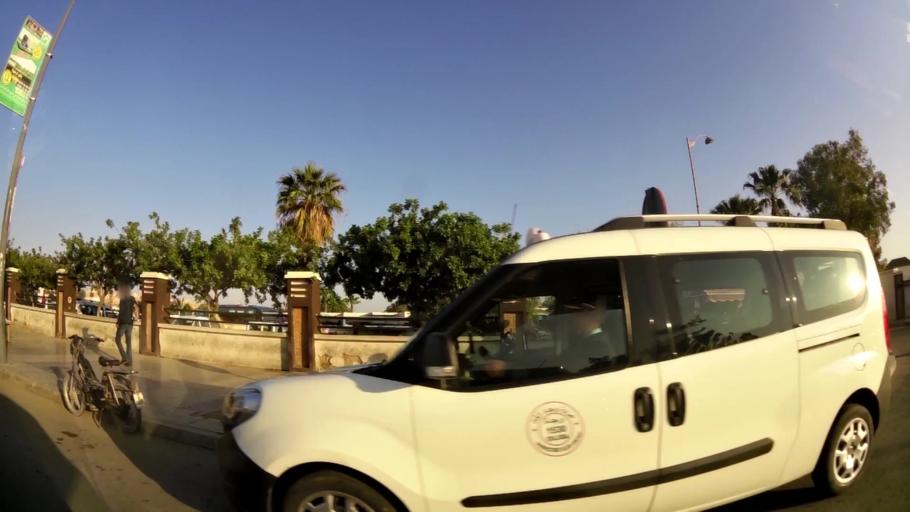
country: MA
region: Oriental
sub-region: Oujda-Angad
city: Oujda
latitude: 34.6753
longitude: -1.9301
